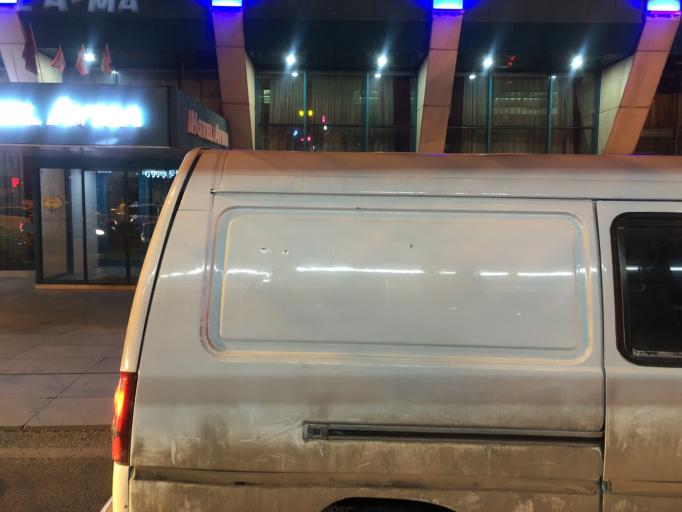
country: TR
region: Ankara
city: Cankaya
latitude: 39.9185
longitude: 32.8585
